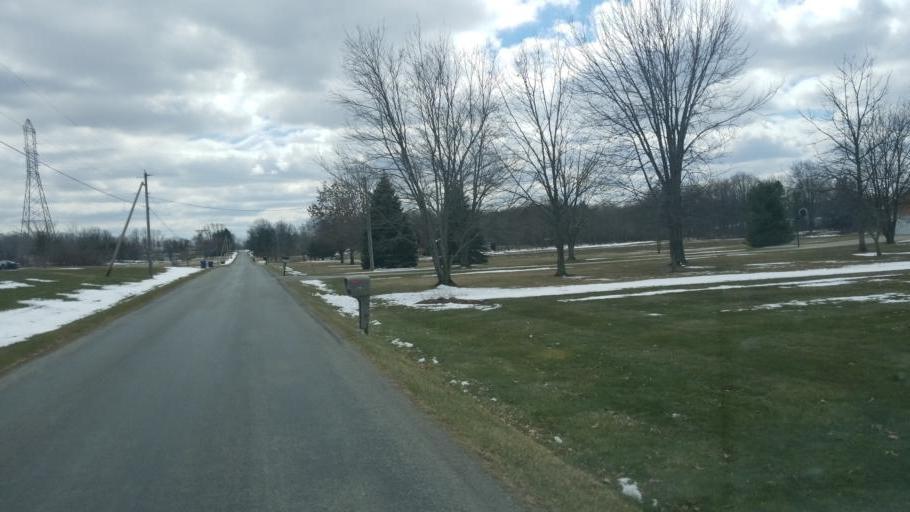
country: US
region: Ohio
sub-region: Richland County
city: Shelby
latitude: 40.8554
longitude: -82.5980
